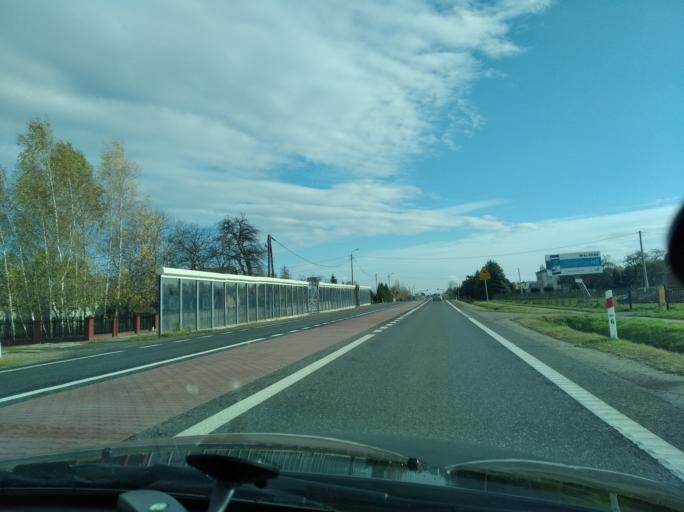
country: PL
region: Subcarpathian Voivodeship
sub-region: Powiat debicki
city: Brzeznica
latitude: 50.0624
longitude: 21.5210
